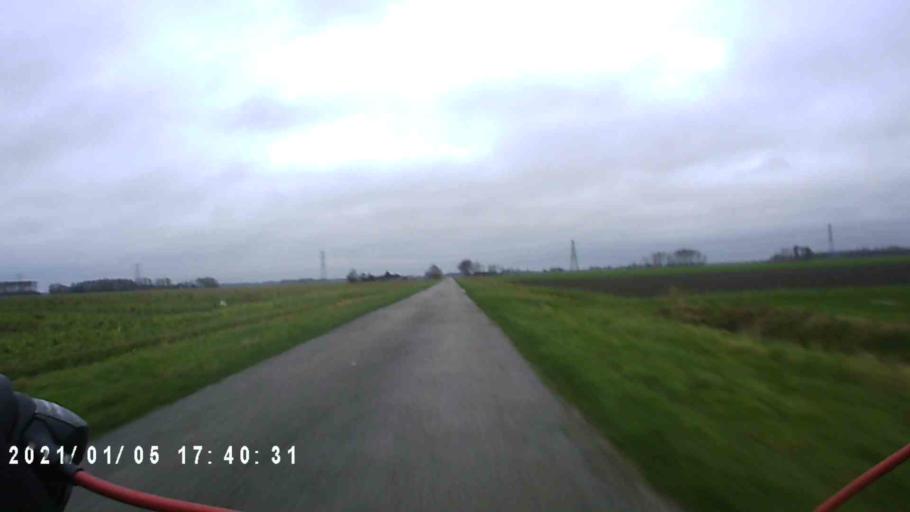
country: NL
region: Groningen
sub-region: Gemeente Delfzijl
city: Delfzijl
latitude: 53.2252
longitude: 6.9172
